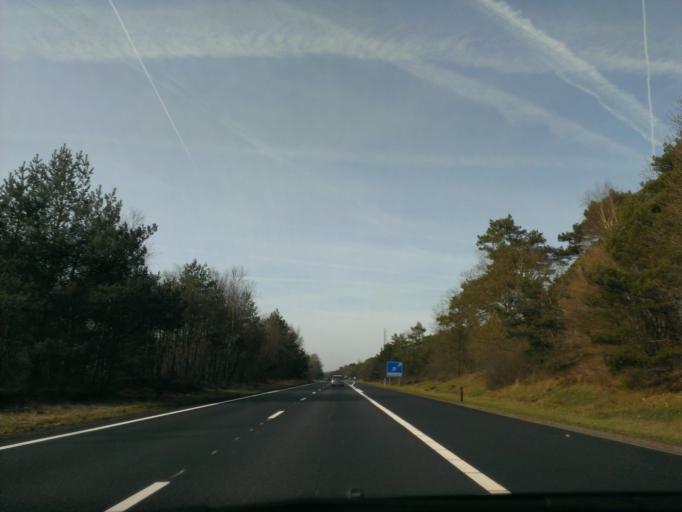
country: NL
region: Gelderland
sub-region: Gemeente Oldebroek
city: Oldebroek
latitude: 52.4241
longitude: 5.9215
